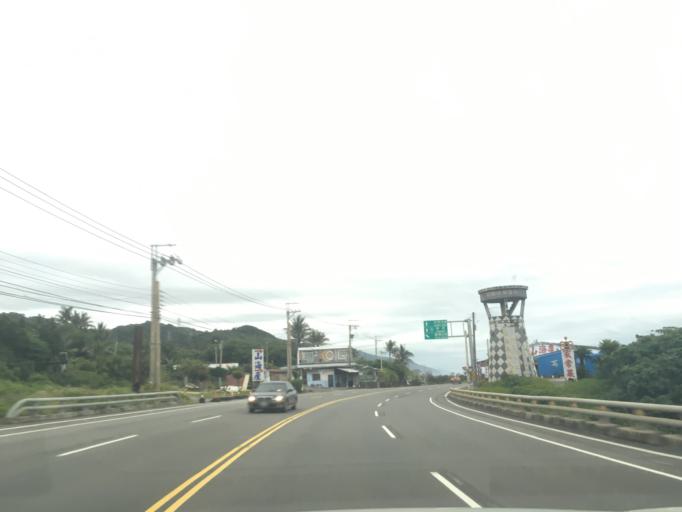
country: TW
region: Taiwan
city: Hengchun
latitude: 22.3029
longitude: 120.8889
